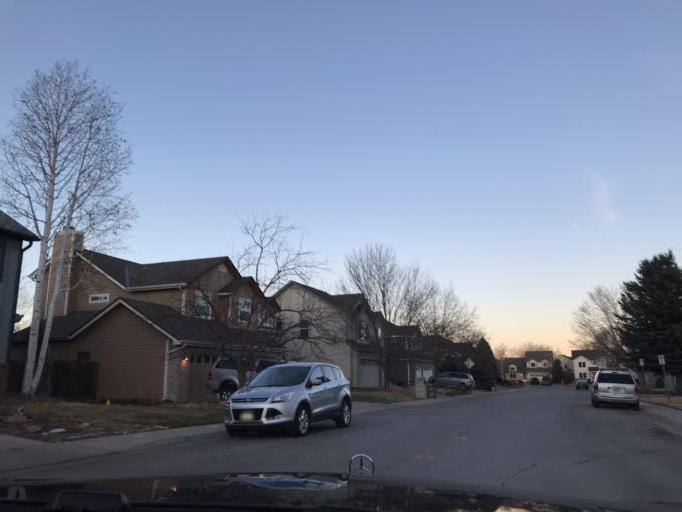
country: US
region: Colorado
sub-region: Jefferson County
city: Applewood
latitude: 39.8230
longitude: -105.1643
